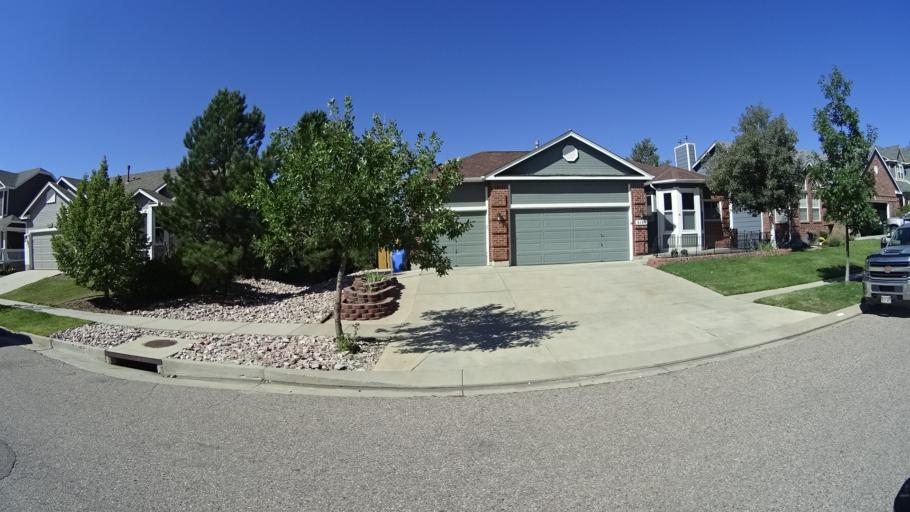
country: US
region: Colorado
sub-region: El Paso County
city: Black Forest
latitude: 38.9508
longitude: -104.7268
